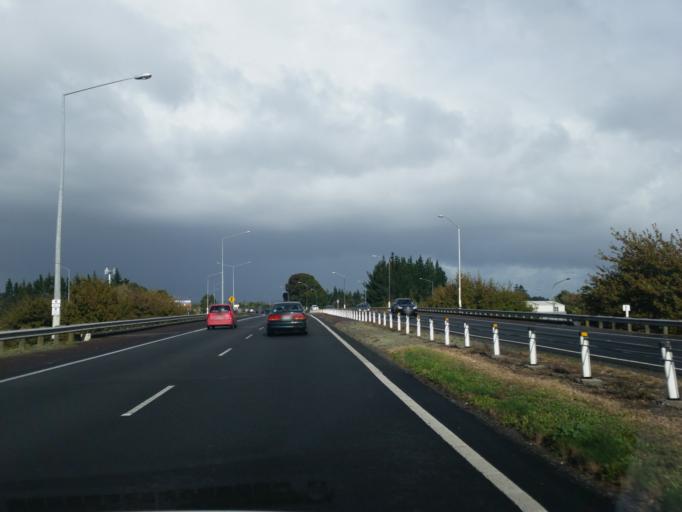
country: NZ
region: Auckland
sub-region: Auckland
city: Papakura
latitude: -37.1070
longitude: 174.9461
